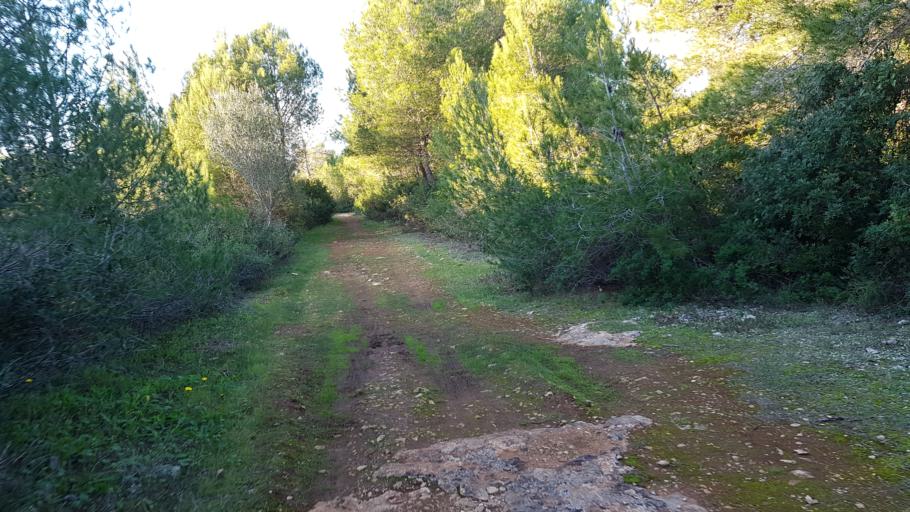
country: IT
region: Apulia
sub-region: Provincia di Lecce
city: Nardo
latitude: 40.1502
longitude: 17.9672
